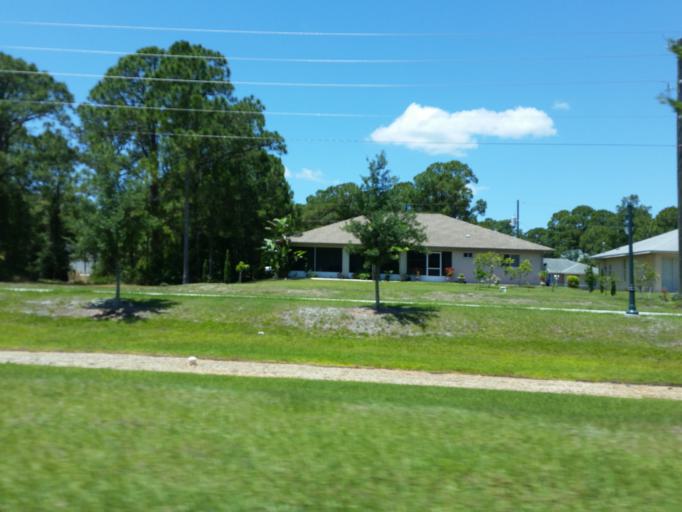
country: US
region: Florida
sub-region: Sarasota County
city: North Port
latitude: 27.0791
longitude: -82.2091
